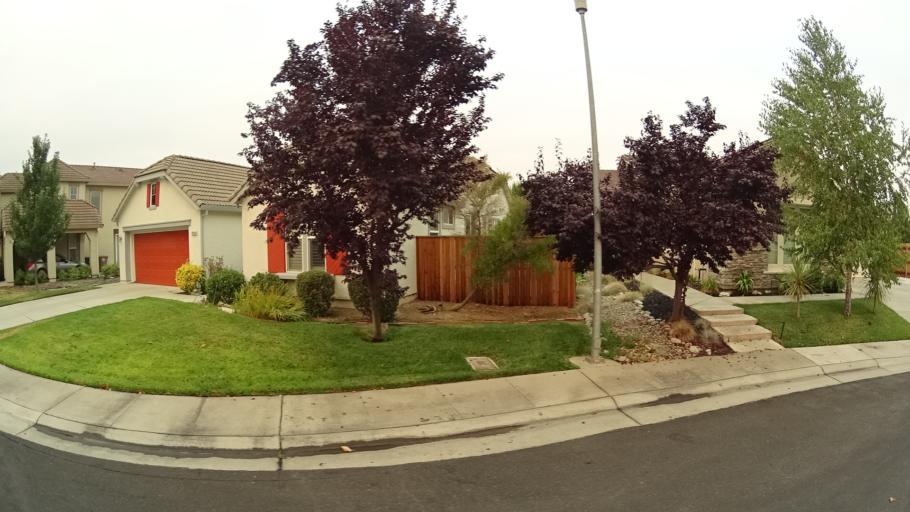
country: US
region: California
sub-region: Sacramento County
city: Laguna
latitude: 38.3851
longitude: -121.4366
